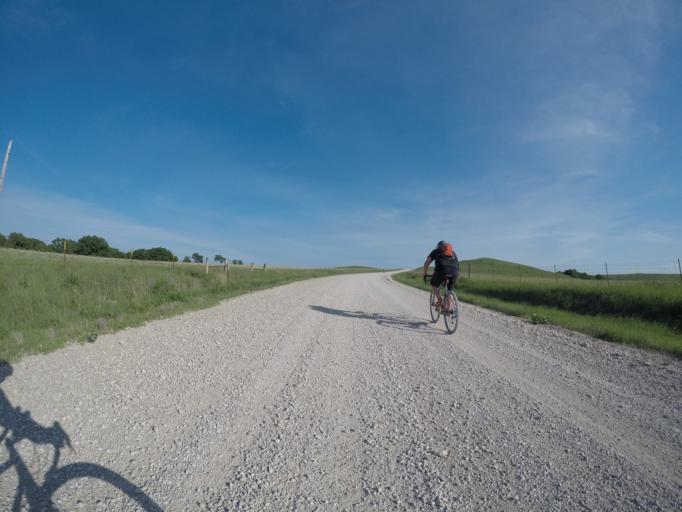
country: US
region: Kansas
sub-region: Riley County
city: Manhattan
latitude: 39.0566
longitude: -96.4966
